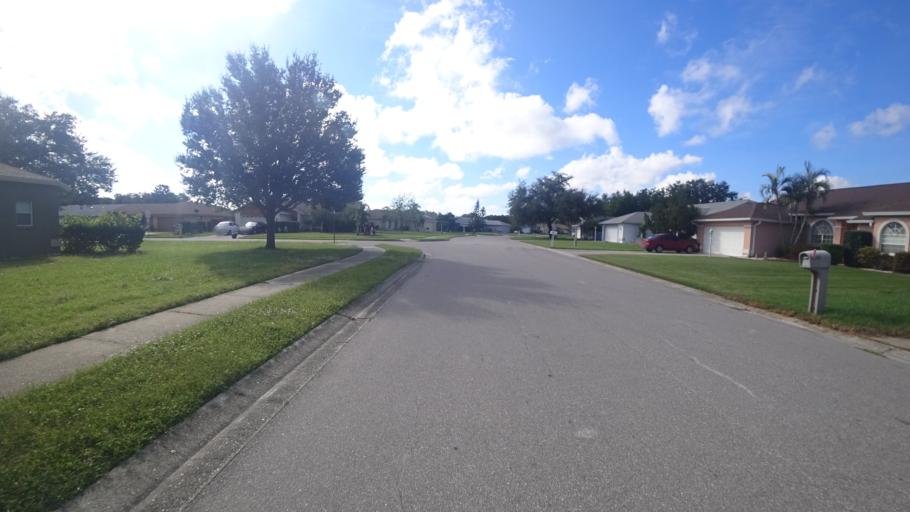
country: US
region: Florida
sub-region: Manatee County
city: Ellenton
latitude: 27.5729
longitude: -82.4947
